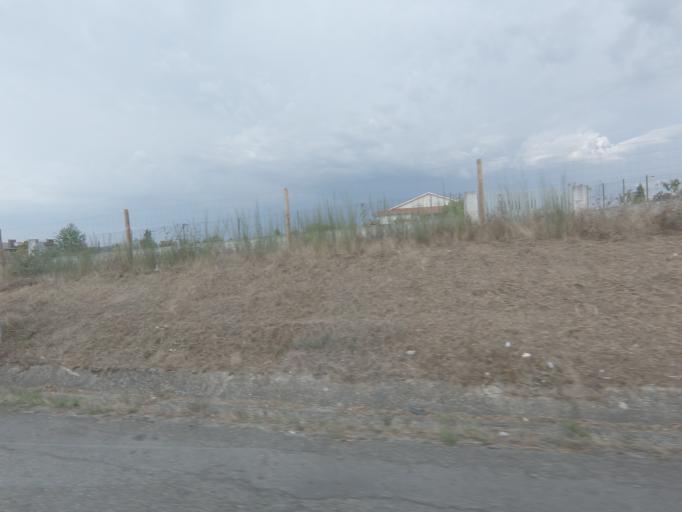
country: PT
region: Viseu
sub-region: Concelho de Tondela
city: Tondela
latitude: 40.5160
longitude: -8.0931
